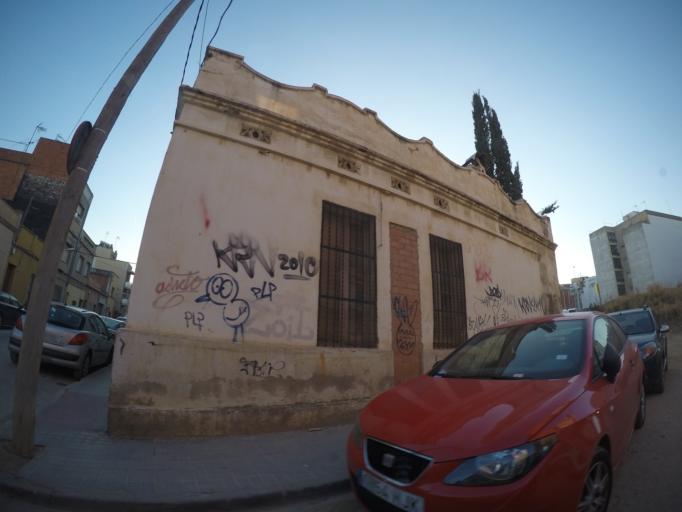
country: ES
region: Catalonia
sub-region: Provincia de Barcelona
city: Badalona
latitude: 41.4497
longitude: 2.2396
